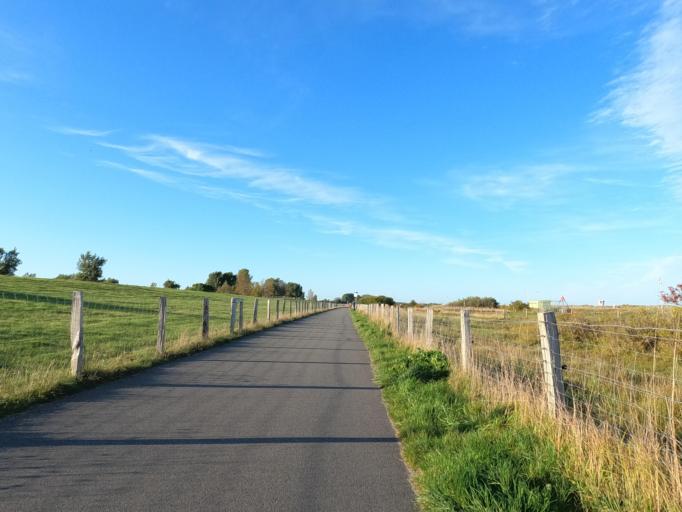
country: DE
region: Schleswig-Holstein
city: Dahme
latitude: 54.2361
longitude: 11.0831
